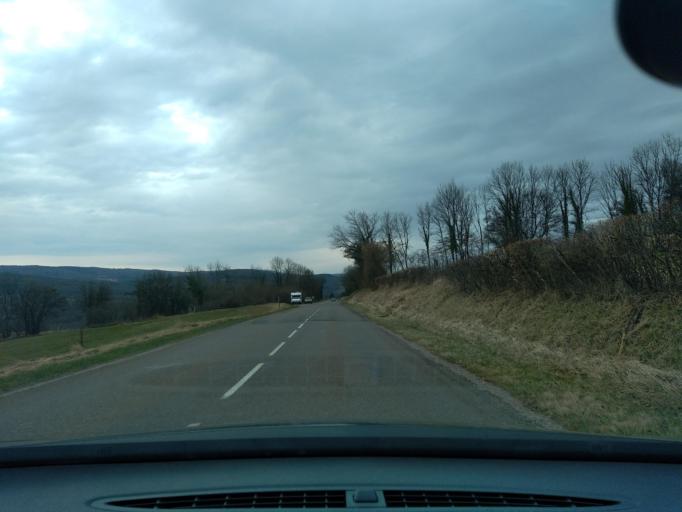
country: FR
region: Franche-Comte
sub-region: Departement du Jura
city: Orgelet
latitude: 46.5000
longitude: 5.5873
